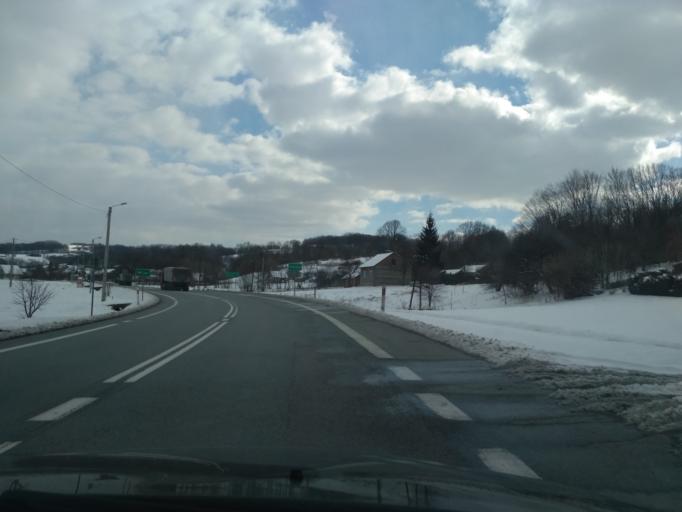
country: PL
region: Subcarpathian Voivodeship
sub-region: Powiat strzyzowski
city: Polomia
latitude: 49.9069
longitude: 21.8658
